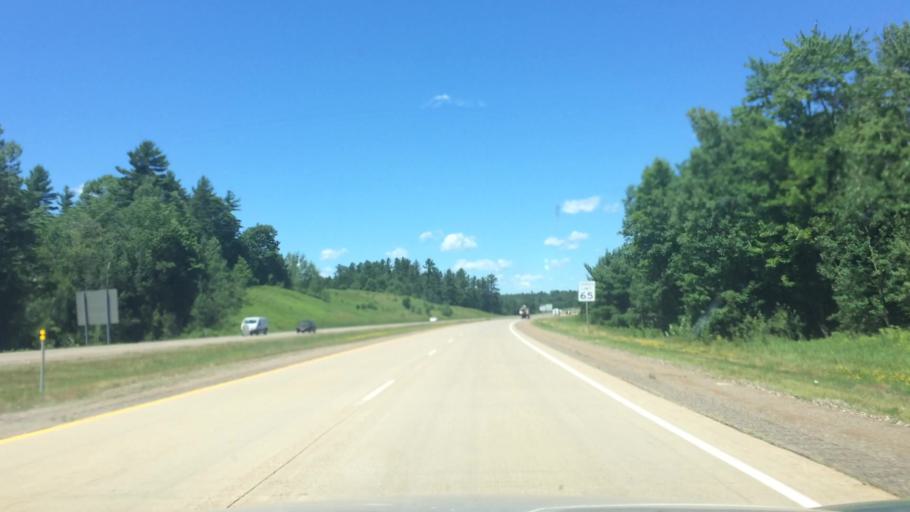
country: US
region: Wisconsin
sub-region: Lincoln County
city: Tomahawk
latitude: 45.4263
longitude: -89.6764
